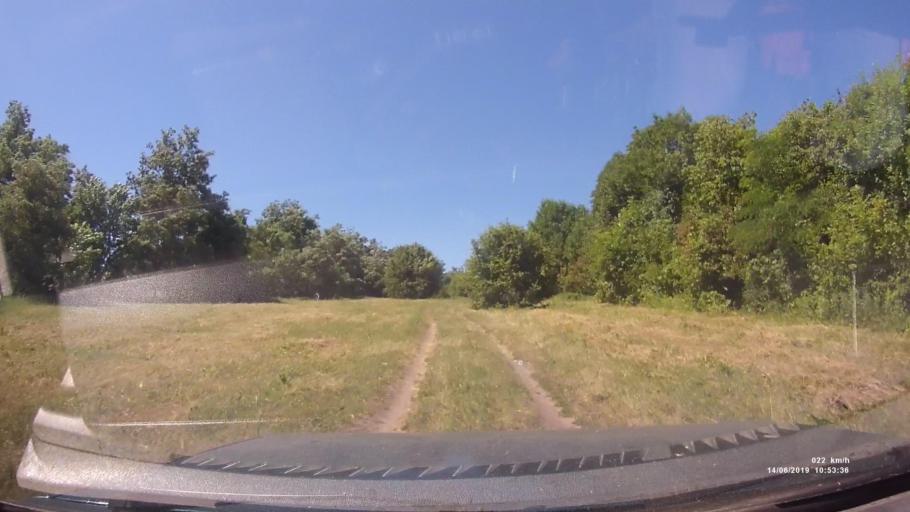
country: RU
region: Rostov
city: Kazanskaya
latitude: 49.8633
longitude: 41.3806
